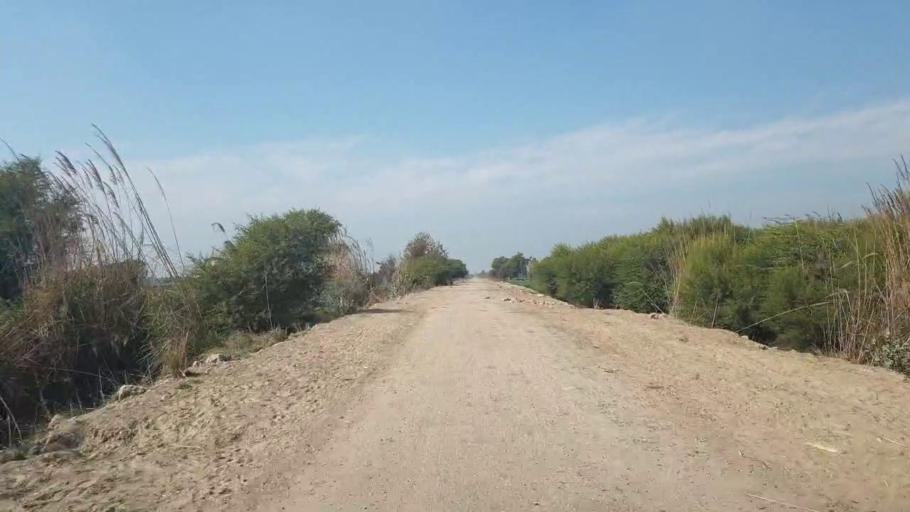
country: PK
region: Sindh
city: Shahdadpur
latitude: 25.9926
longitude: 68.5304
